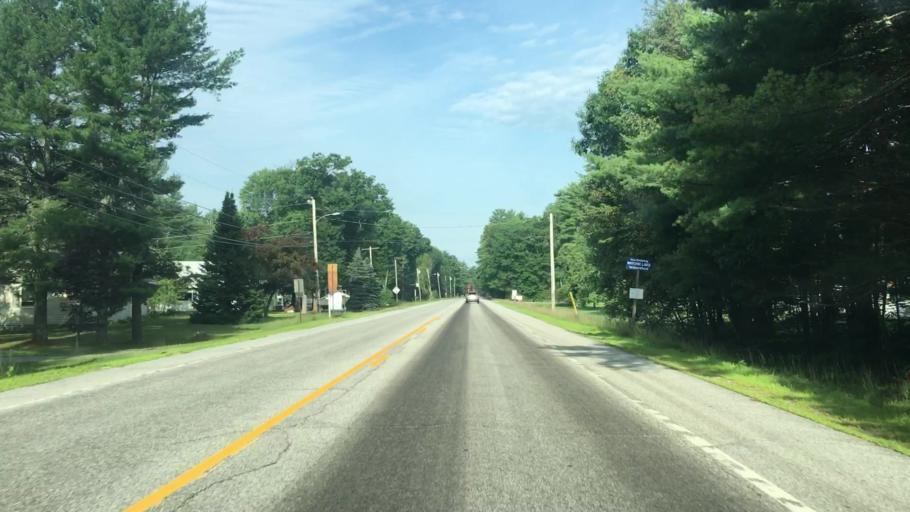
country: US
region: Maine
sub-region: Cumberland County
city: Steep Falls
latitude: 43.7321
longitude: -70.5933
